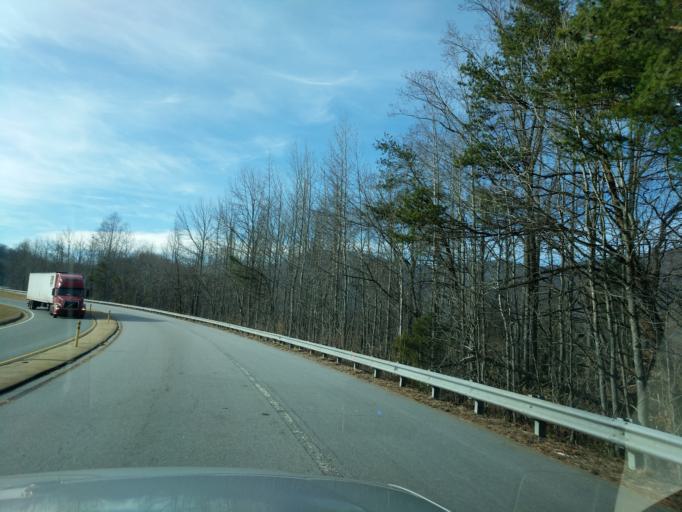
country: US
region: North Carolina
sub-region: Polk County
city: Columbus
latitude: 35.2524
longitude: -82.2096
